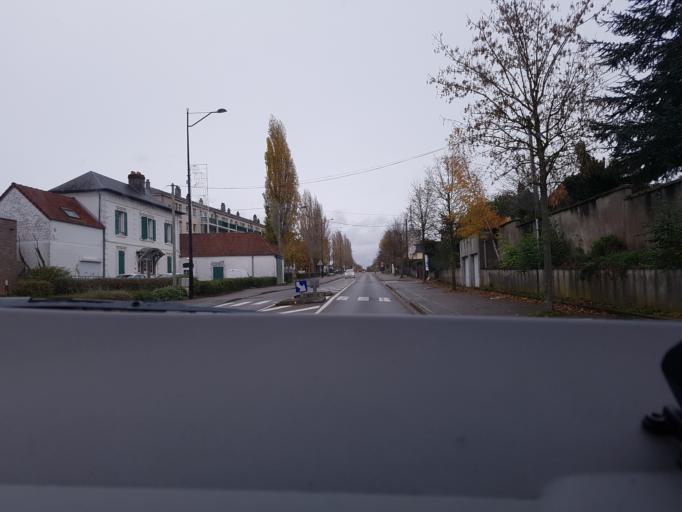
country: FR
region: Picardie
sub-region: Departement de la Somme
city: Abbeville
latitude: 50.1077
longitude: 1.8513
